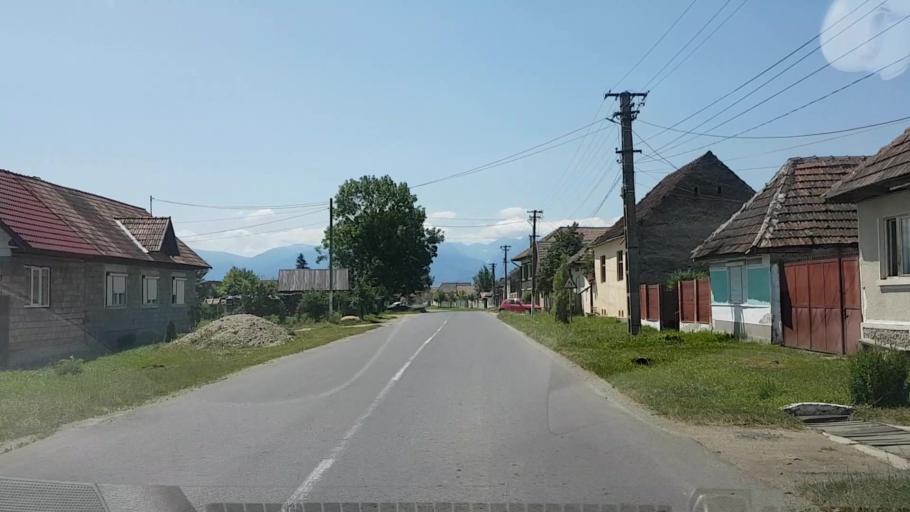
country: RO
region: Brasov
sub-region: Comuna Voila
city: Voila
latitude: 45.8437
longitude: 24.8329
